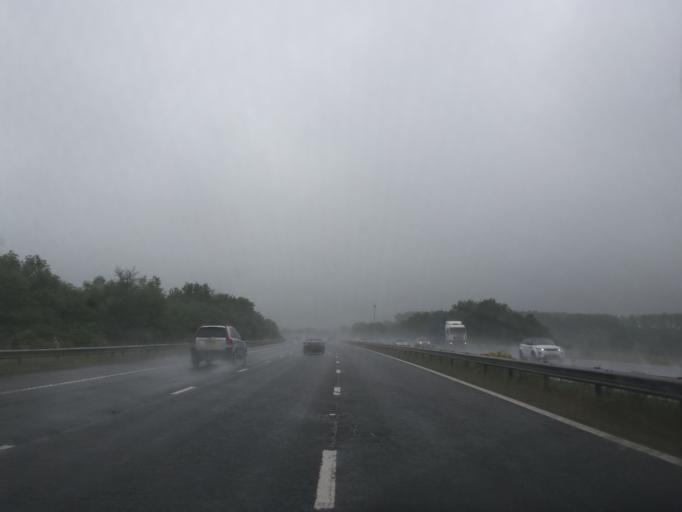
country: GB
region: England
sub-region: Leicestershire
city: Markfield
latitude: 52.6986
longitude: -1.2925
